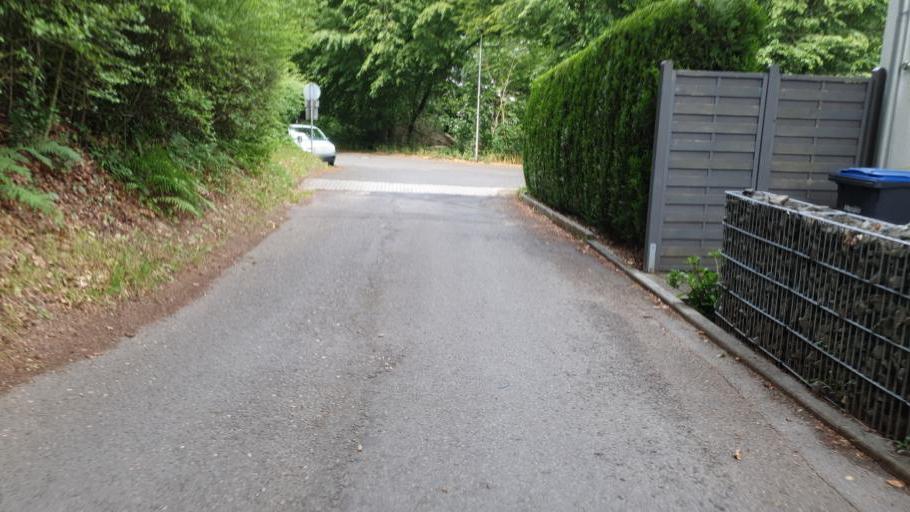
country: DE
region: North Rhine-Westphalia
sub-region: Regierungsbezirk Koln
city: Odenthal
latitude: 51.0152
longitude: 7.0982
